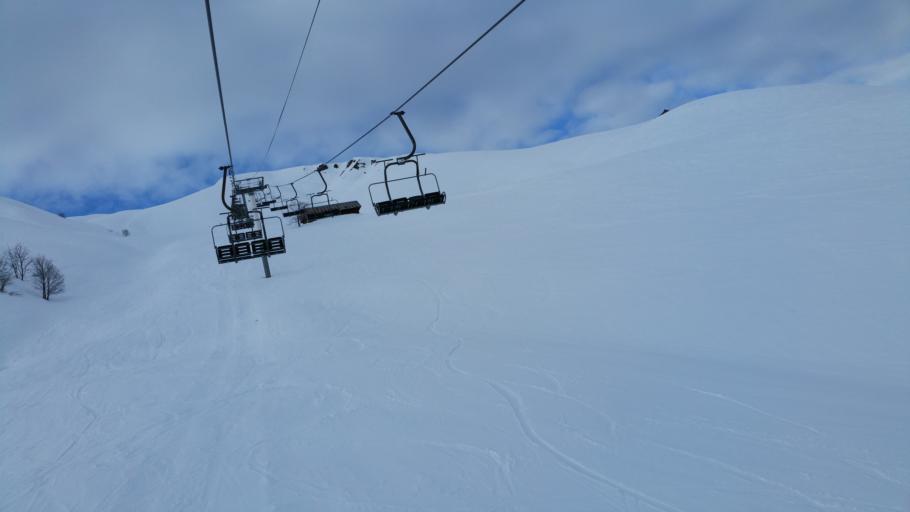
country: FR
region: Rhone-Alpes
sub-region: Departement de la Savoie
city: Saint-Etienne-de-Cuines
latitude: 45.2646
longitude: 6.2637
